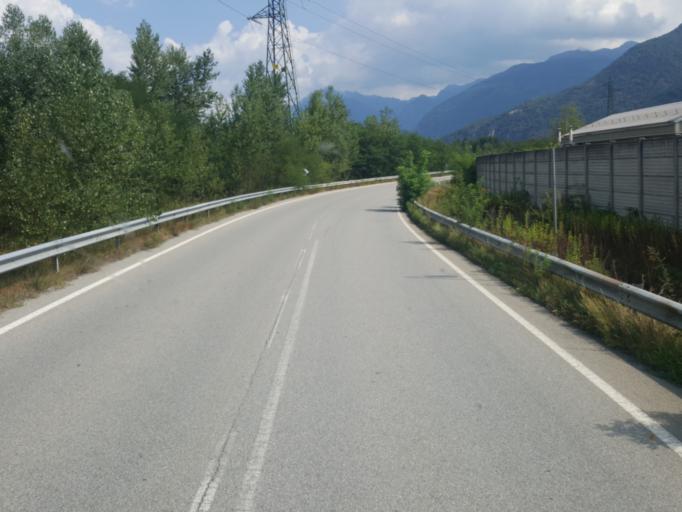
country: IT
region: Piedmont
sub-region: Provincia Verbano-Cusio-Ossola
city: Beura
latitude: 46.0788
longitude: 8.2866
